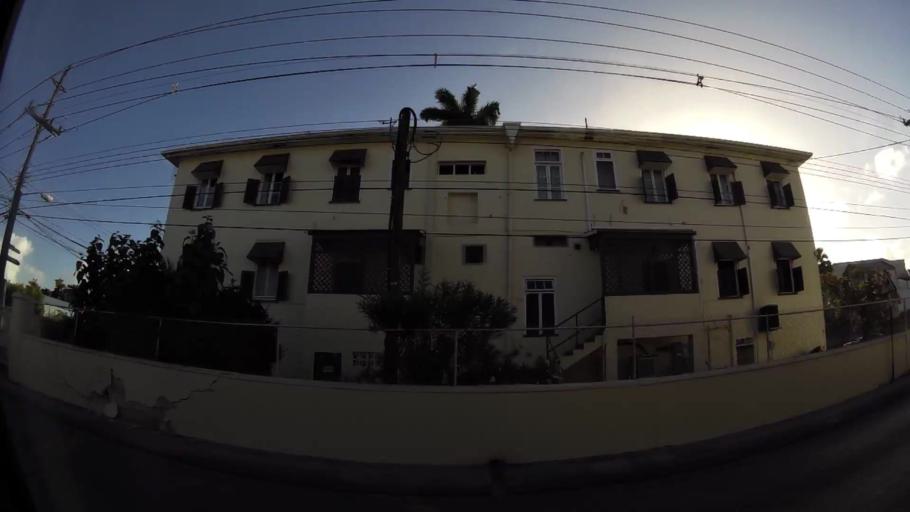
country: BB
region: Saint Michael
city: Bridgetown
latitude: 13.0813
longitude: -59.6077
